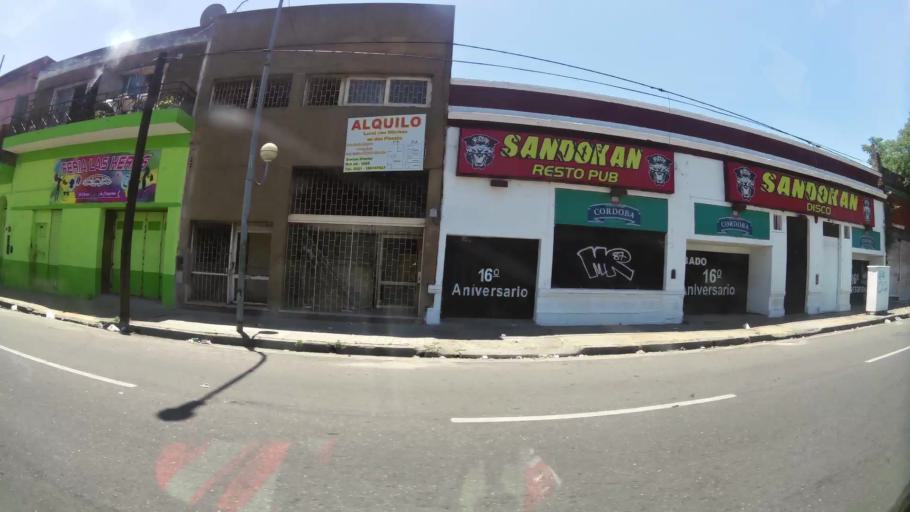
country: AR
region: Cordoba
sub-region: Departamento de Capital
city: Cordoba
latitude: -31.4059
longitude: -64.1775
